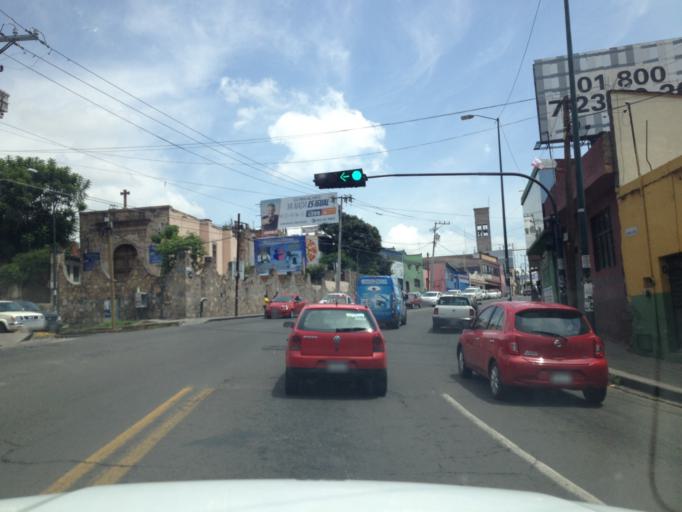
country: MX
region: Michoacan
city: Morelia
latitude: 19.7150
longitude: -101.1891
